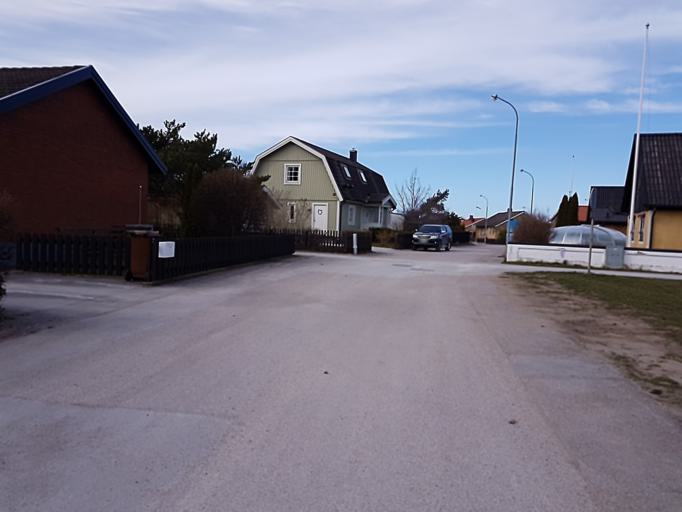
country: SE
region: Gotland
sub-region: Gotland
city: Visby
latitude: 57.6344
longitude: 18.3187
